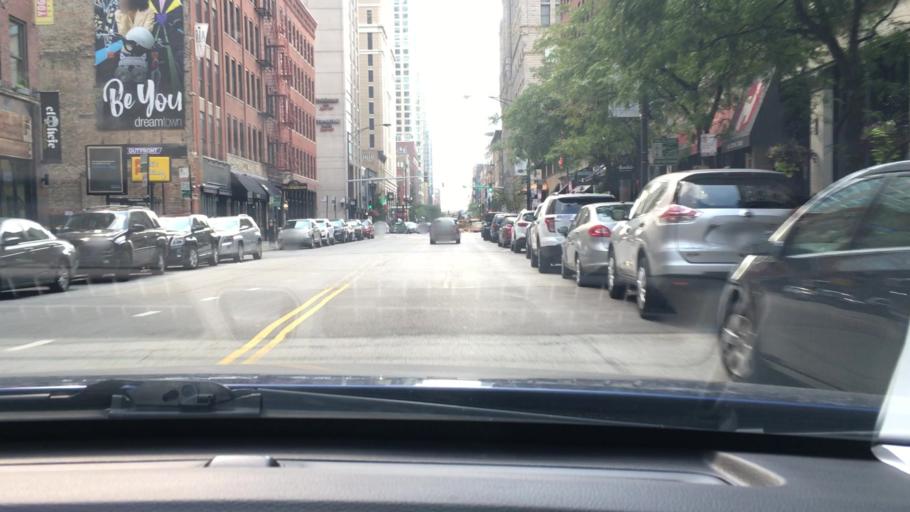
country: US
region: Illinois
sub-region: Cook County
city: Chicago
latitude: 41.8900
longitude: -87.6283
